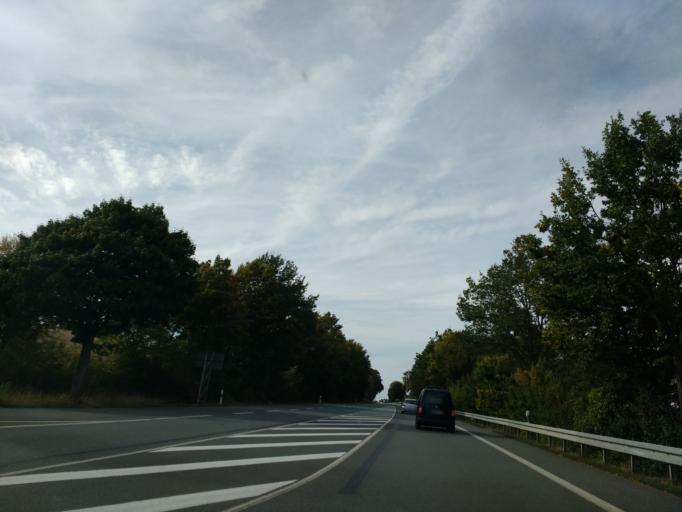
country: DE
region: North Rhine-Westphalia
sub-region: Regierungsbezirk Detmold
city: Nieheim
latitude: 51.8015
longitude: 9.1336
